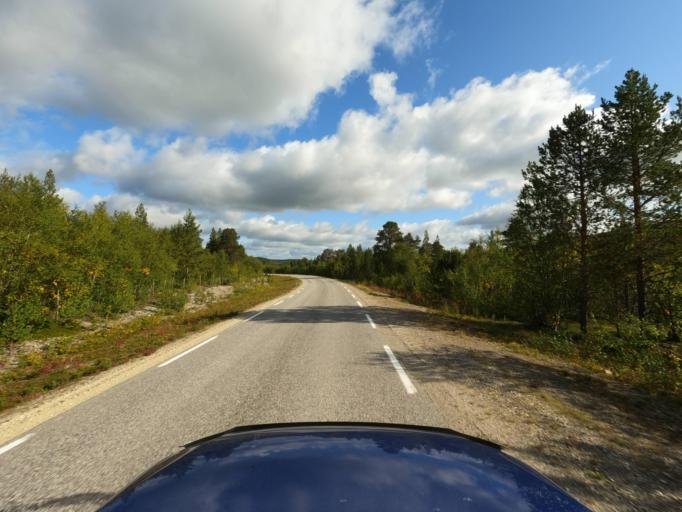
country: NO
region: Finnmark Fylke
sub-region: Karasjok
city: Karasjohka
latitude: 69.4285
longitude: 24.9515
